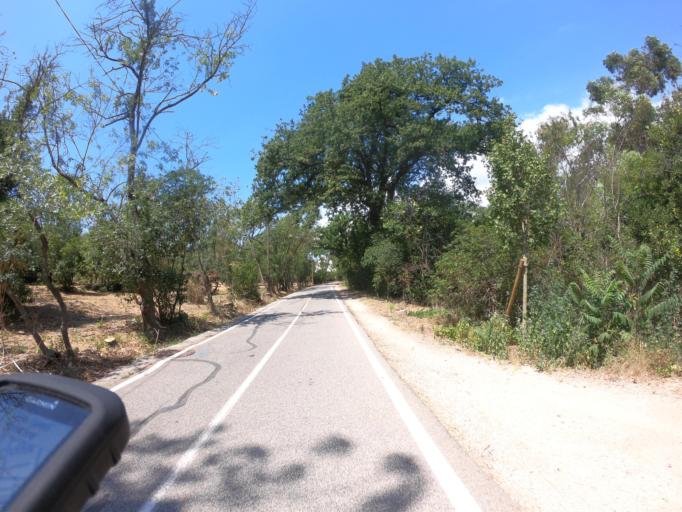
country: FR
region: Provence-Alpes-Cote d'Azur
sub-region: Departement du Var
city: La Valette-du-Var
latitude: 43.1167
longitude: 5.9743
